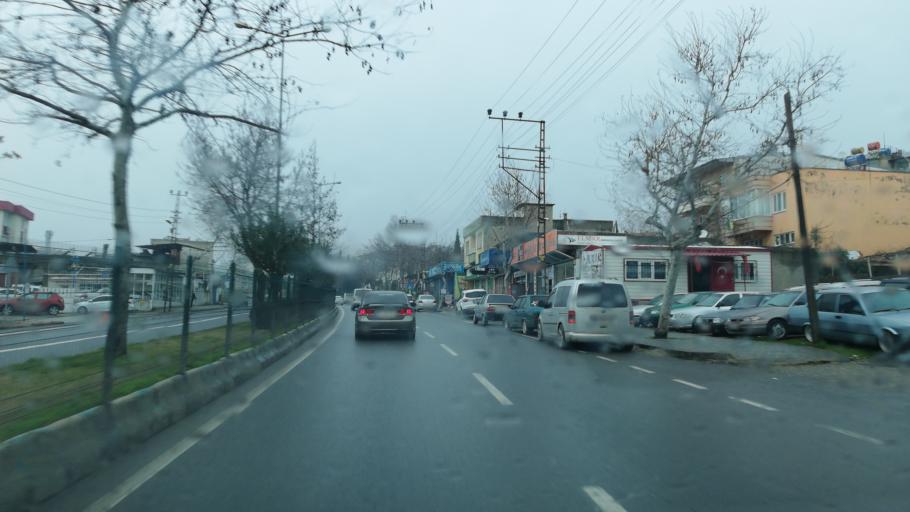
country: TR
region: Kahramanmaras
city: Kahramanmaras
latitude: 37.5695
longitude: 36.9464
